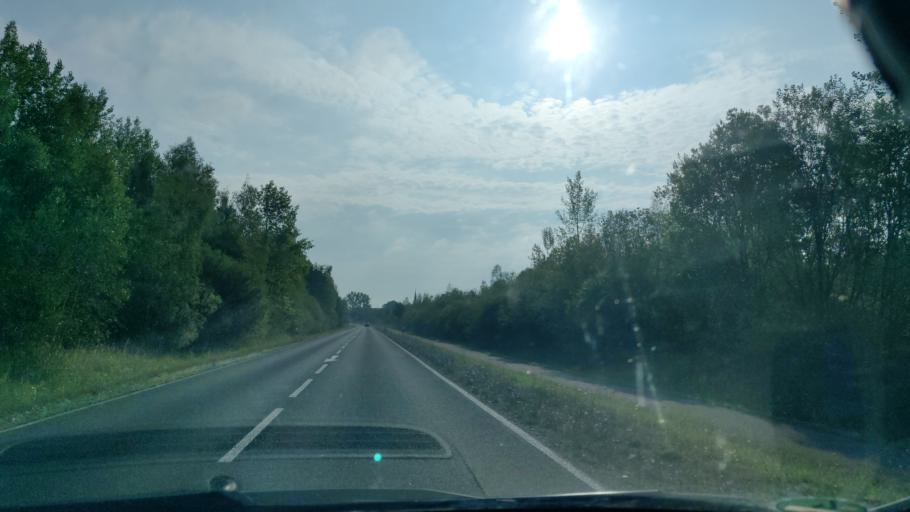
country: DE
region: Saxony
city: Frohburg
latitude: 51.0973
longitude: 12.5505
